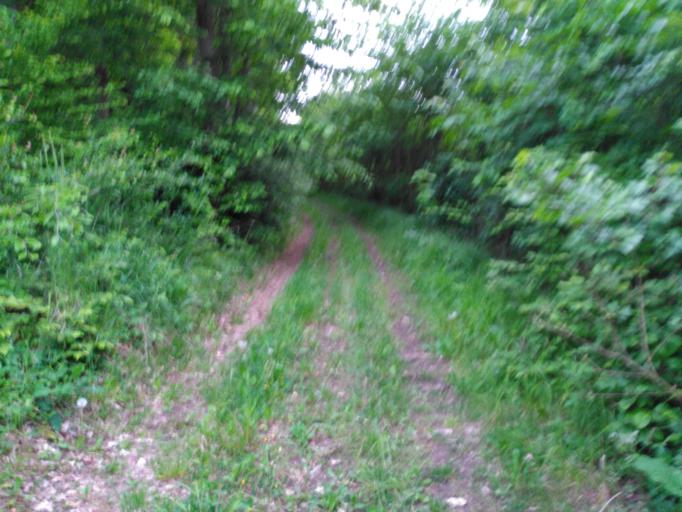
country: CZ
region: Central Bohemia
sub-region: Okres Beroun
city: Beroun
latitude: 49.9092
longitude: 14.0930
